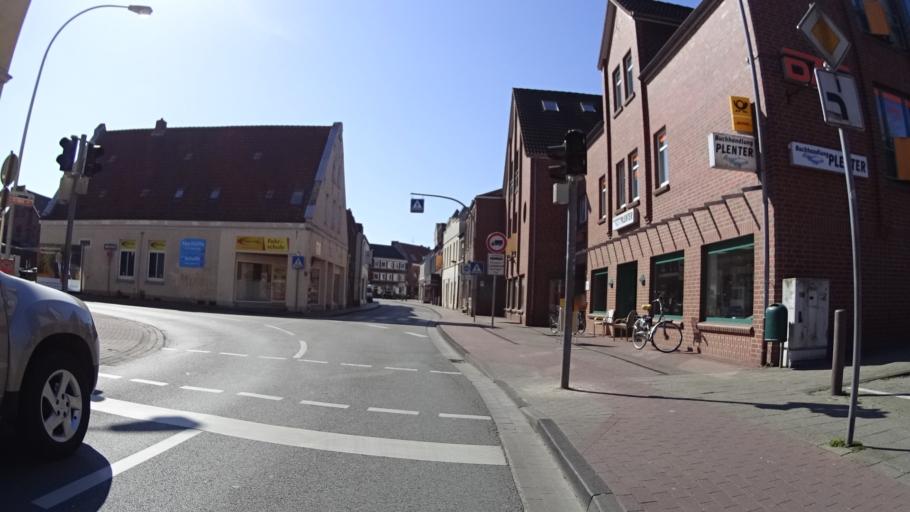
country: DE
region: Lower Saxony
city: Leer
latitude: 53.2305
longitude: 7.4514
